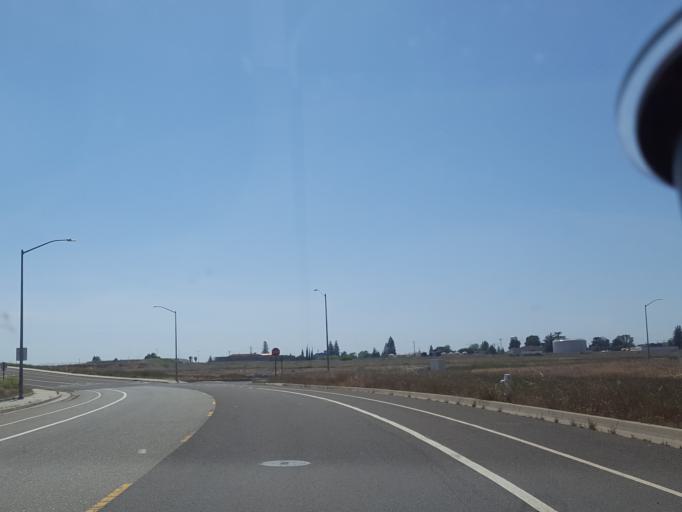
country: US
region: California
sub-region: Sacramento County
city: Rancho Cordova
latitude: 38.5690
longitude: -121.2808
